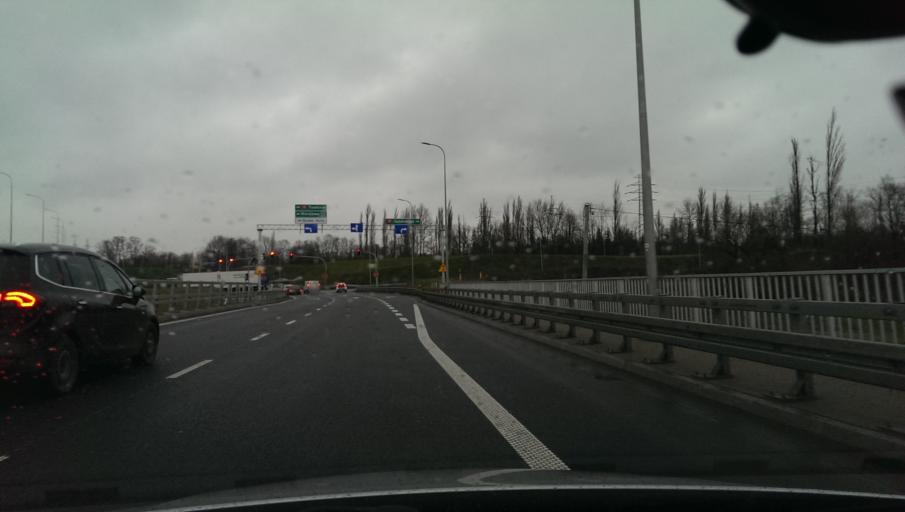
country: PL
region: Lesser Poland Voivodeship
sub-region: Powiat wielicki
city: Kokotow
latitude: 50.0628
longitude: 20.0747
